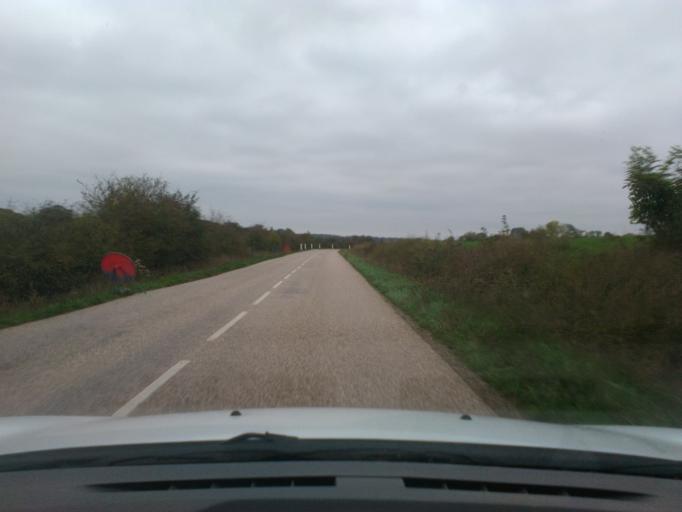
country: FR
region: Lorraine
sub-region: Departement des Vosges
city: Dogneville
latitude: 48.2634
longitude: 6.5045
